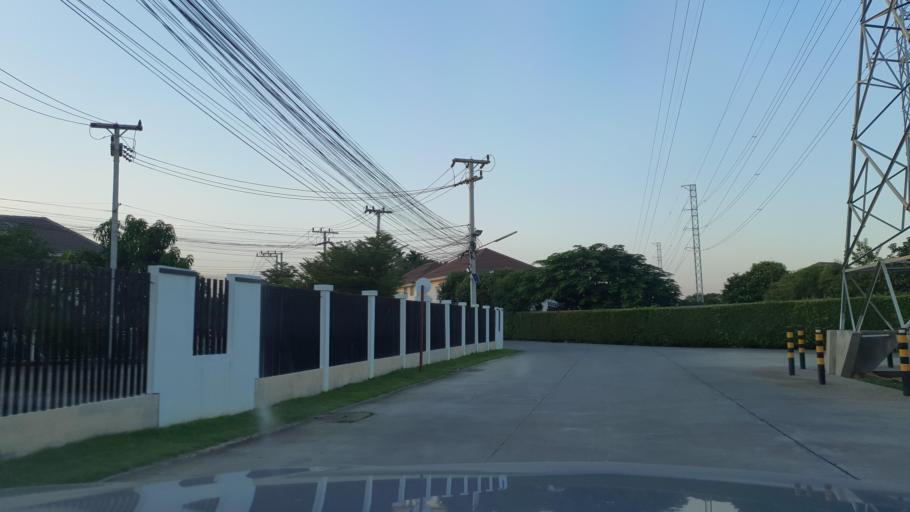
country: TH
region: Chiang Mai
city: Saraphi
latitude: 18.7312
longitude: 99.0756
